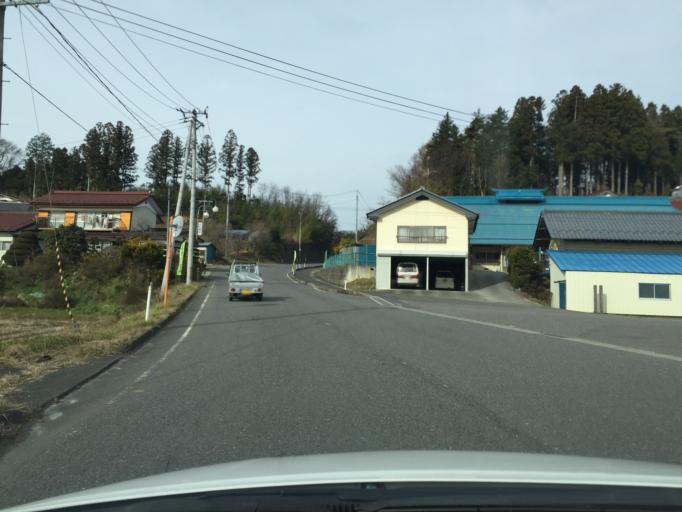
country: JP
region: Fukushima
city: Funehikimachi-funehiki
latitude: 37.4027
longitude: 140.5934
